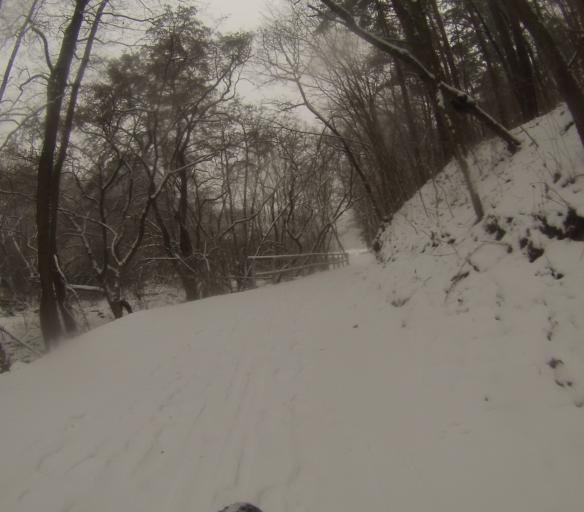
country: CZ
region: South Moravian
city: Strelice
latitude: 49.1337
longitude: 16.4943
